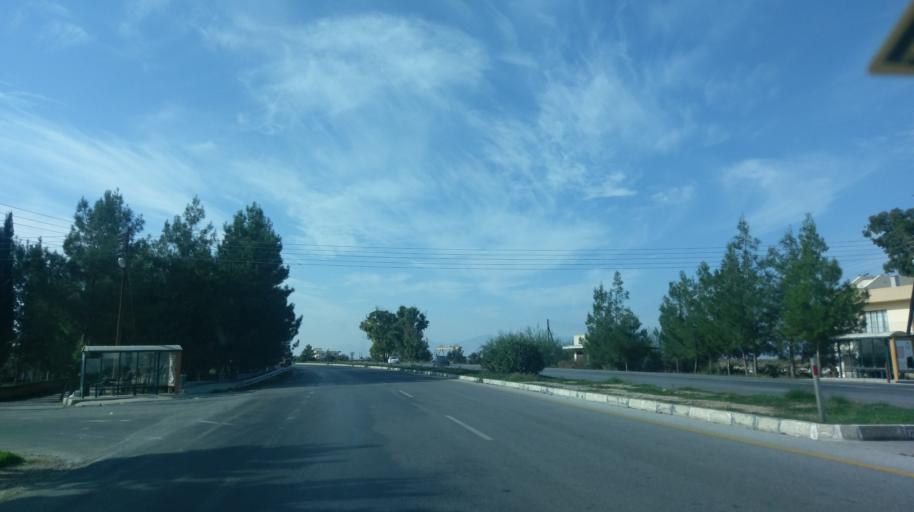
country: CY
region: Ammochostos
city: Lefkonoiko
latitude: 35.1775
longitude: 33.7583
